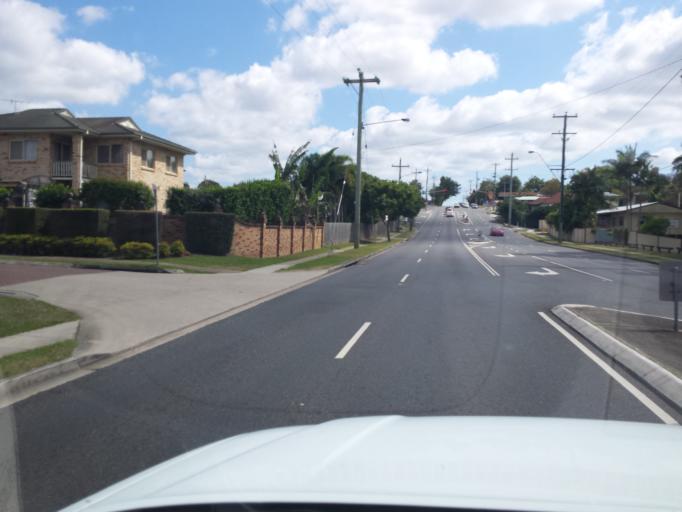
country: AU
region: Queensland
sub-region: Brisbane
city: Zillmere
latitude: -27.3687
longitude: 153.0364
